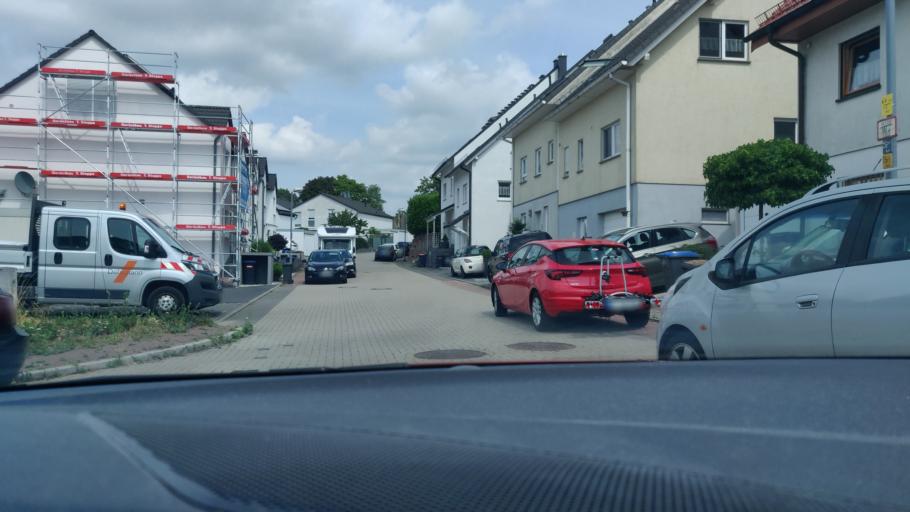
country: DE
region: North Rhine-Westphalia
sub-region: Regierungsbezirk Dusseldorf
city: Velbert
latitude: 51.3189
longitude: 7.0681
